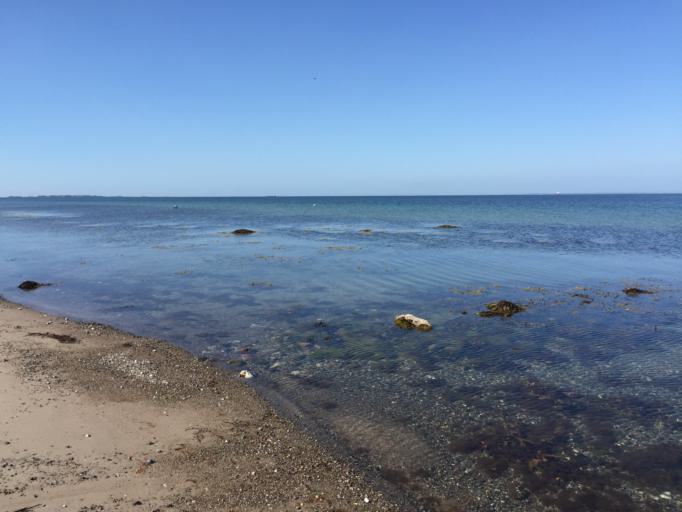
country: DK
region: Zealand
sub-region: Slagelse Kommune
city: Korsor
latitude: 55.2314
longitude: 11.1705
